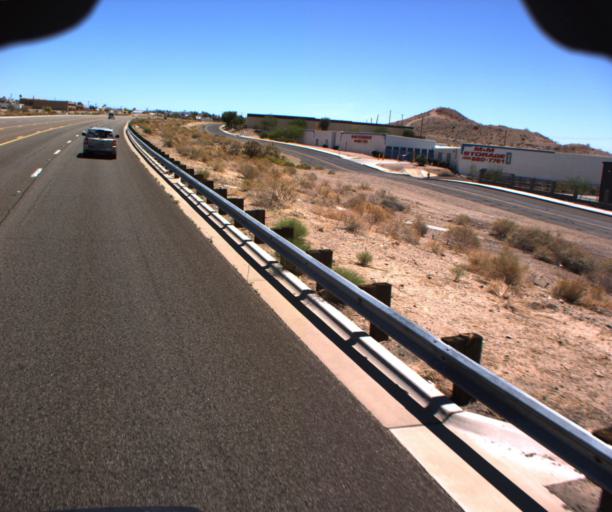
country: US
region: Arizona
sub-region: Mohave County
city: Lake Havasu City
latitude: 34.4574
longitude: -114.2750
